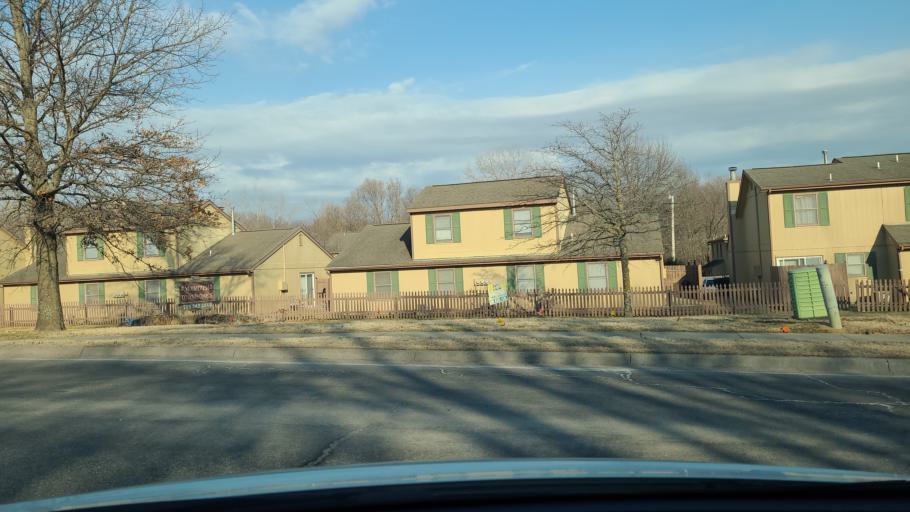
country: US
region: Kansas
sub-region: Douglas County
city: Lawrence
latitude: 38.9647
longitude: -95.2884
